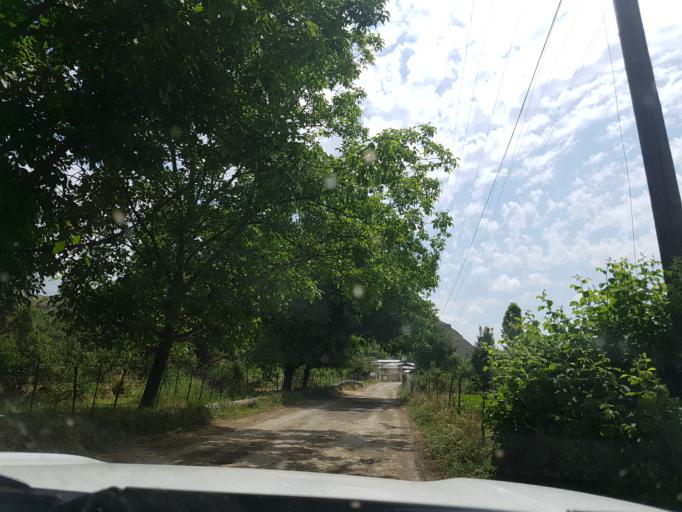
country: TM
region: Ahal
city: Baharly
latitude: 38.2231
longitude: 56.8859
